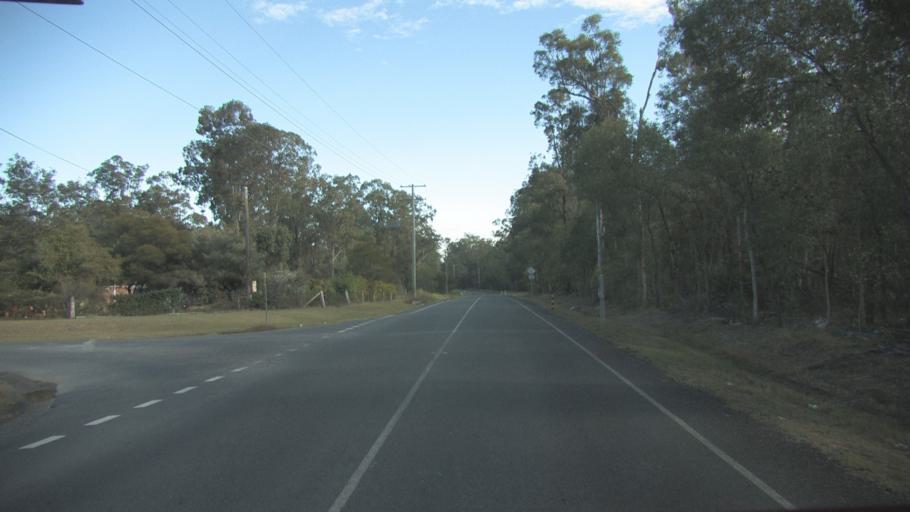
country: AU
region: Queensland
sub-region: Logan
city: North Maclean
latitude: -27.8073
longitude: 153.0603
